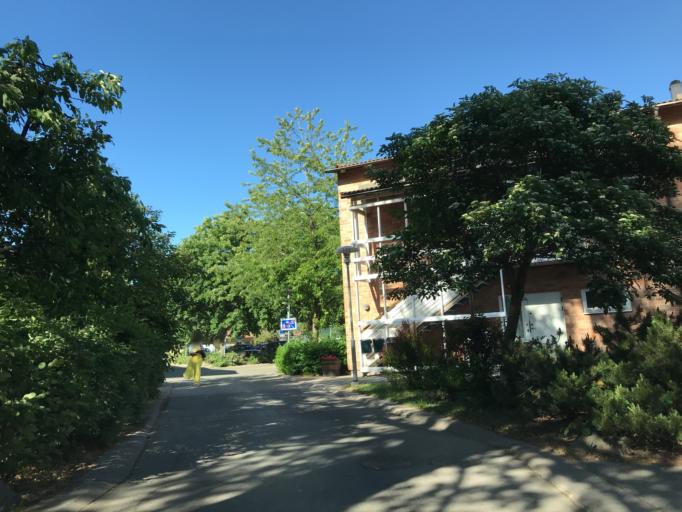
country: SE
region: Stockholm
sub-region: Huddinge Kommun
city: Segeltorp
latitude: 59.2976
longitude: 17.9381
